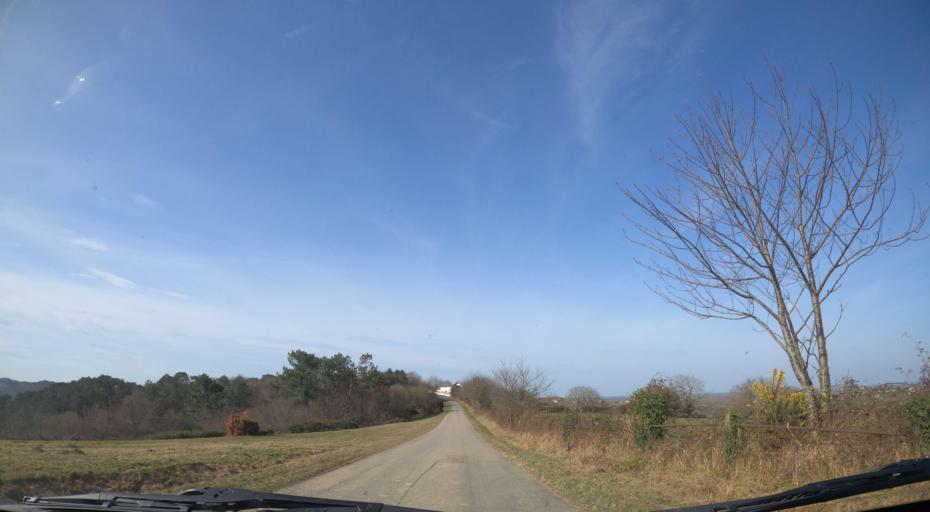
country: FR
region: Aquitaine
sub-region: Departement des Pyrenees-Atlantiques
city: Briscous
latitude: 43.4256
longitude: -1.3706
